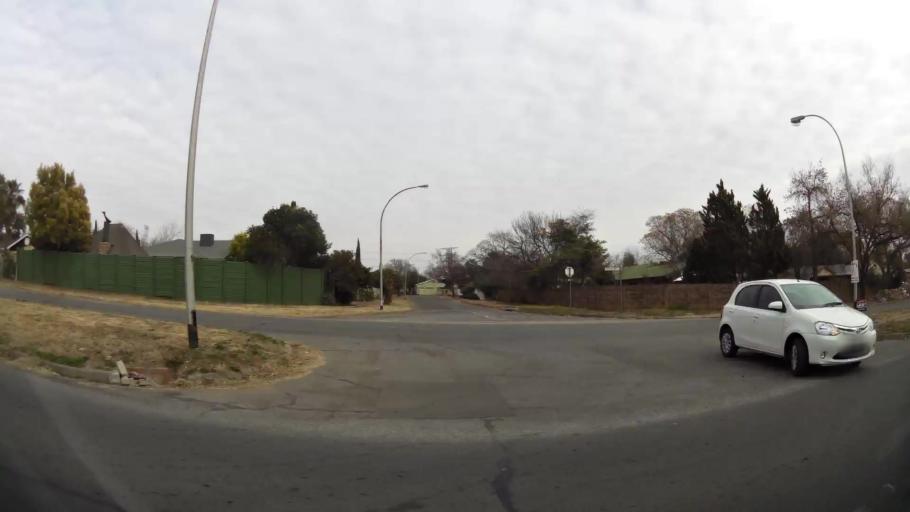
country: ZA
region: Orange Free State
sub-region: Mangaung Metropolitan Municipality
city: Bloemfontein
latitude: -29.1248
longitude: 26.1682
